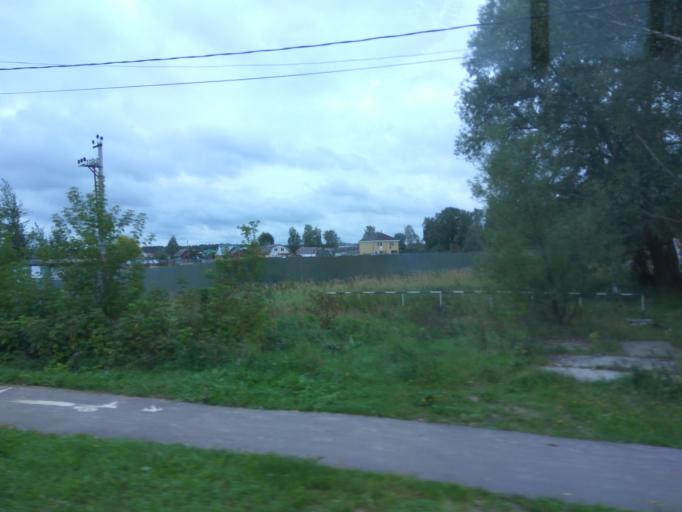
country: RU
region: Moskovskaya
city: Malyshevo
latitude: 55.4988
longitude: 38.3568
